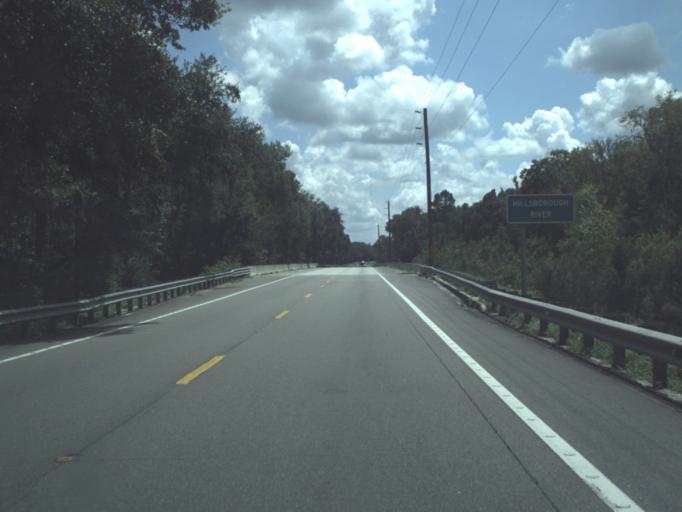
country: US
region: Florida
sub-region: Pasco County
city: Crystal Springs
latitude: 28.1942
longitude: -82.1660
